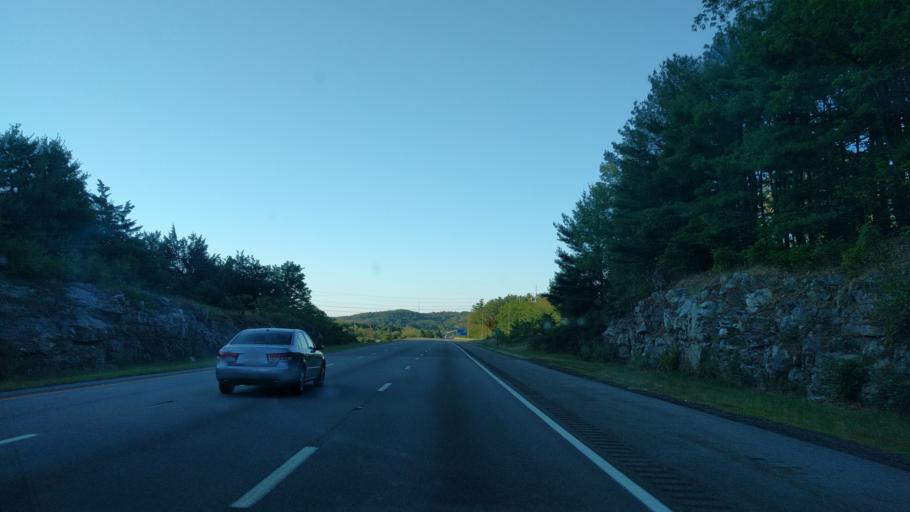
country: US
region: Massachusetts
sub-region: Middlesex County
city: Marlborough
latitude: 42.3201
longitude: -71.5712
